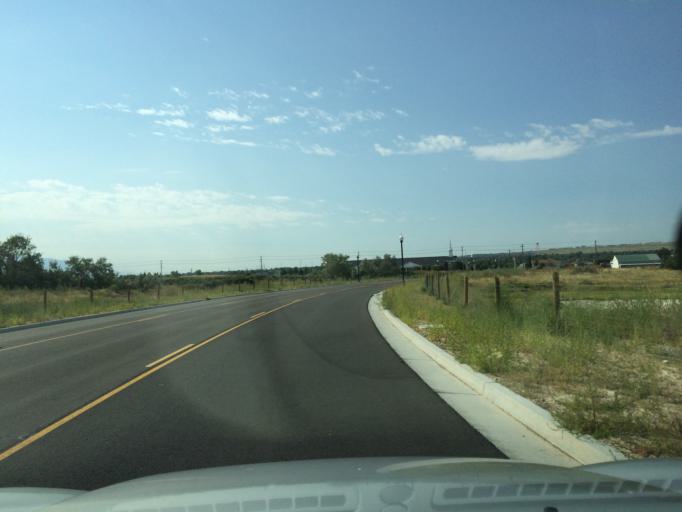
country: US
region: Utah
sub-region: Salt Lake County
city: West Valley City
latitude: 40.7127
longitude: -112.0444
